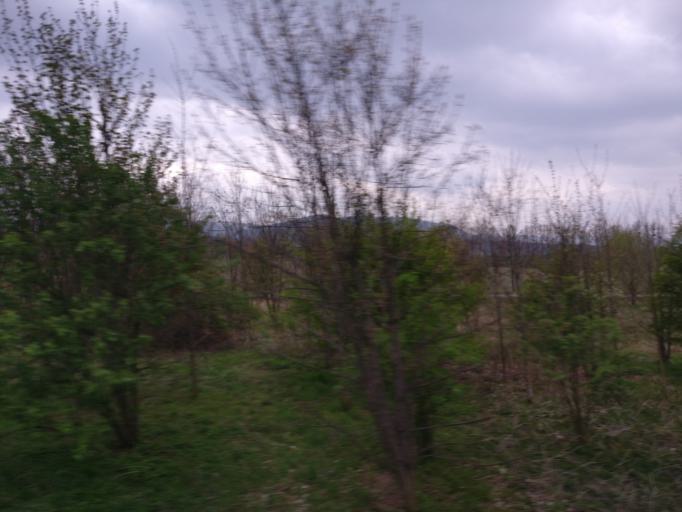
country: DE
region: Saxony-Anhalt
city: Stapelburg
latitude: 51.9164
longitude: 10.6678
